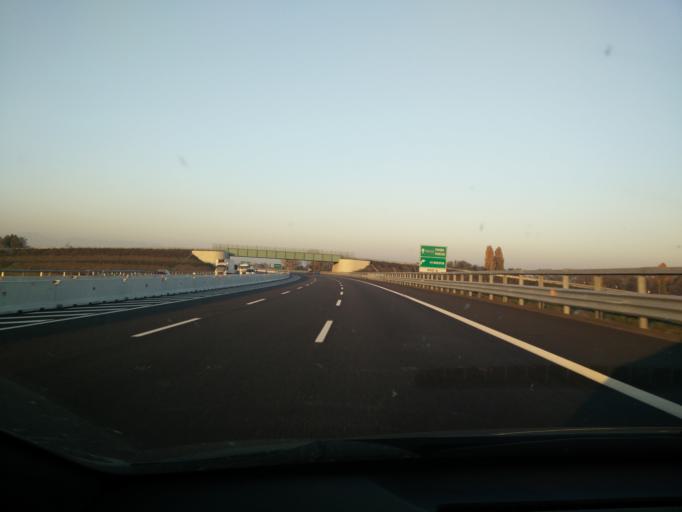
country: IT
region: Lombardy
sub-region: Citta metropolitana di Milano
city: Melzo
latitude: 45.4911
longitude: 9.4419
